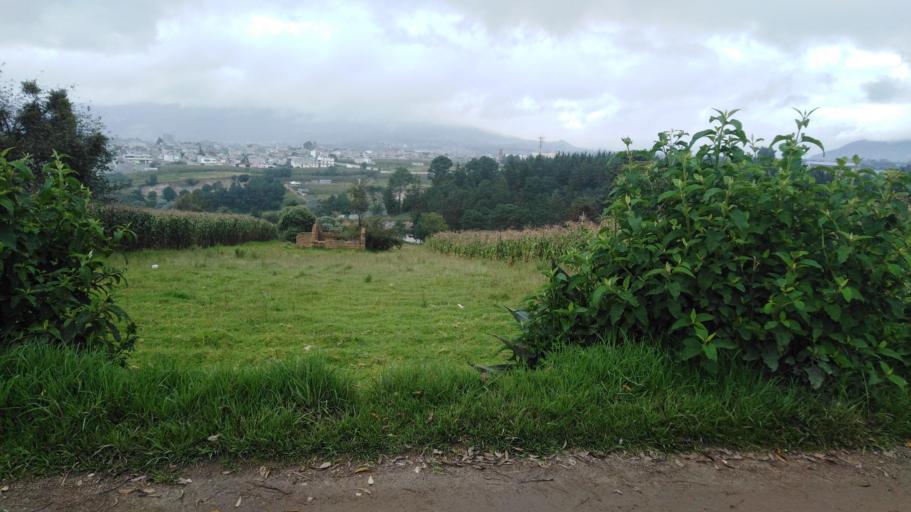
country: GT
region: Quetzaltenango
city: Quetzaltenango
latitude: 14.8570
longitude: -91.5012
